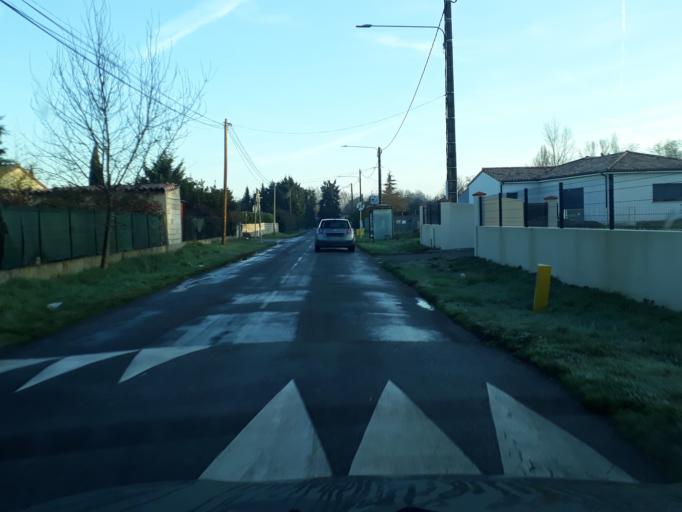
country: FR
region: Midi-Pyrenees
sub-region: Departement de la Haute-Garonne
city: Longages
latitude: 43.3466
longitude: 1.2358
